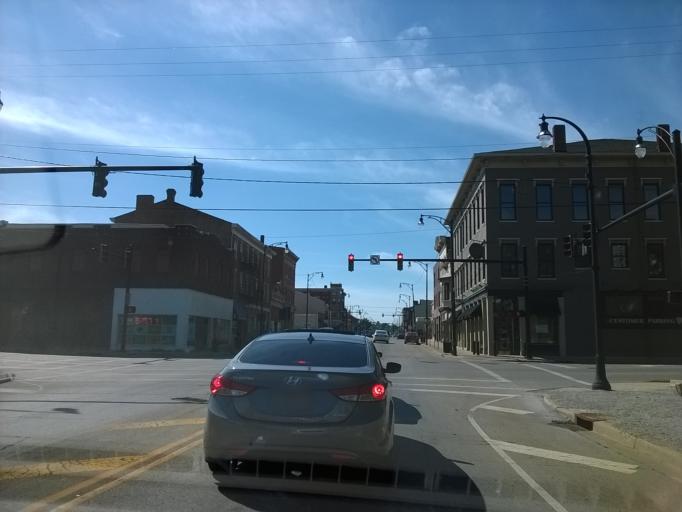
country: US
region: Ohio
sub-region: Butler County
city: Hamilton
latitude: 39.4023
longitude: -84.5667
